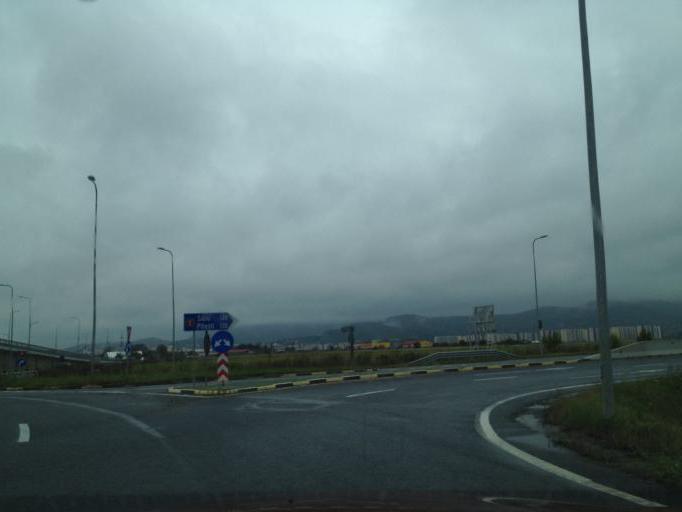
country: RO
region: Brasov
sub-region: Comuna Ghimbav
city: Ghimbav
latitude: 45.6785
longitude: 25.5552
